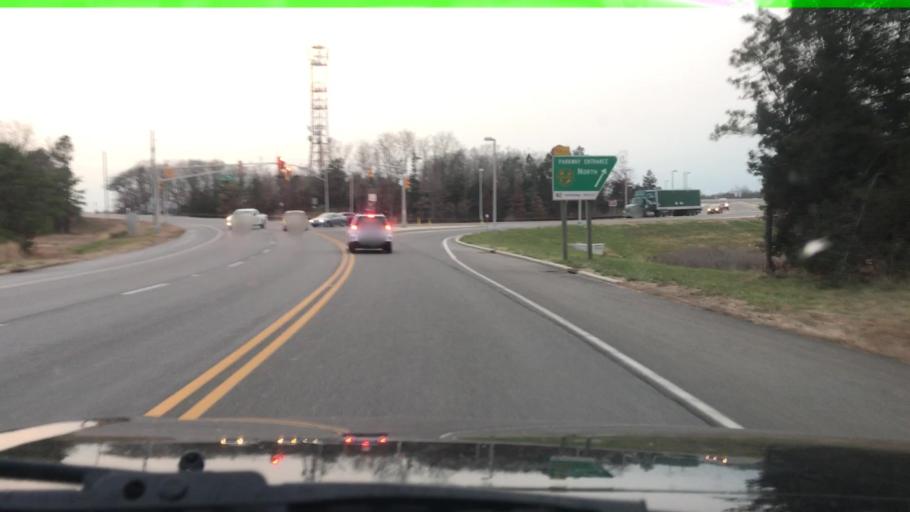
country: US
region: New Jersey
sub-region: Ocean County
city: Silver Ridge
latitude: 39.9899
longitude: -74.2067
